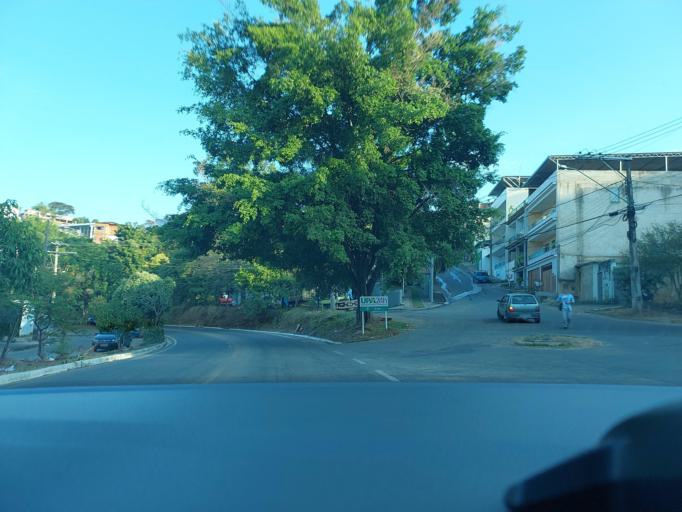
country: BR
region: Minas Gerais
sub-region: Muriae
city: Muriae
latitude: -21.1270
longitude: -42.4030
